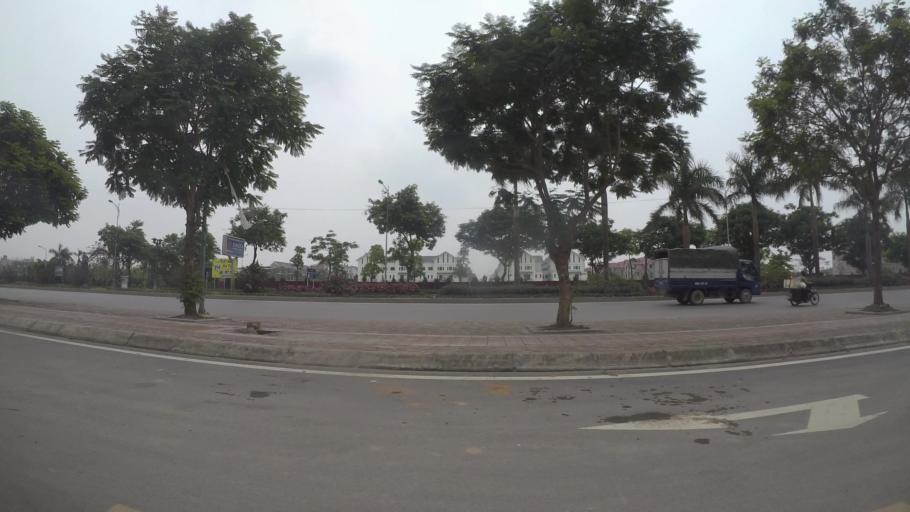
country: VN
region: Ha Noi
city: Ha Dong
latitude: 20.9825
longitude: 105.7421
